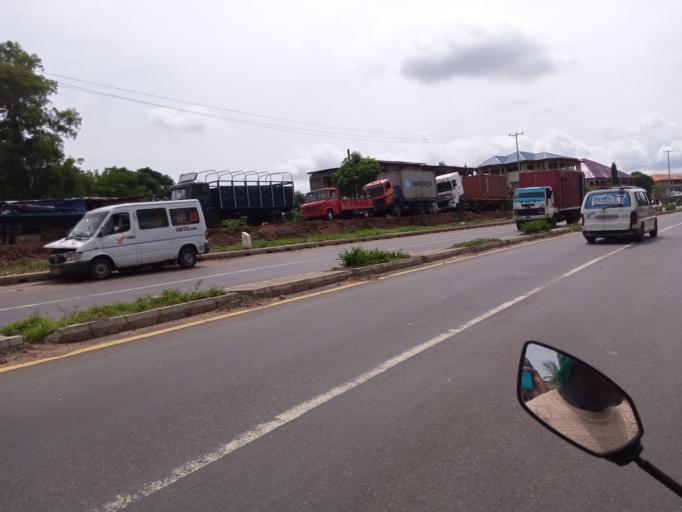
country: SL
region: Western Area
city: Hastings
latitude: 8.3889
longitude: -13.1250
